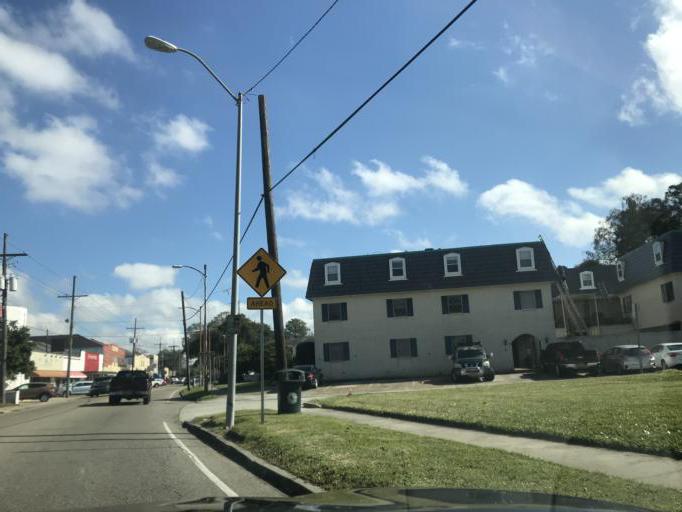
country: US
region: Louisiana
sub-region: Jefferson Parish
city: Metairie
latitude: 29.9849
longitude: -90.1471
